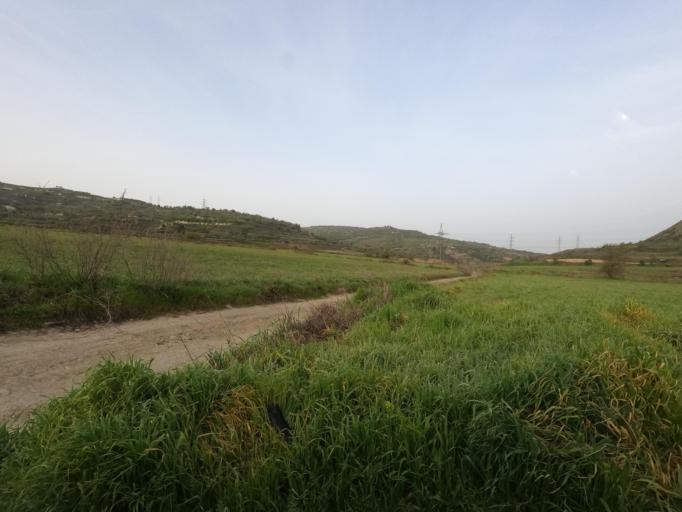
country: CY
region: Pafos
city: Mesogi
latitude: 34.8707
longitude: 32.4931
